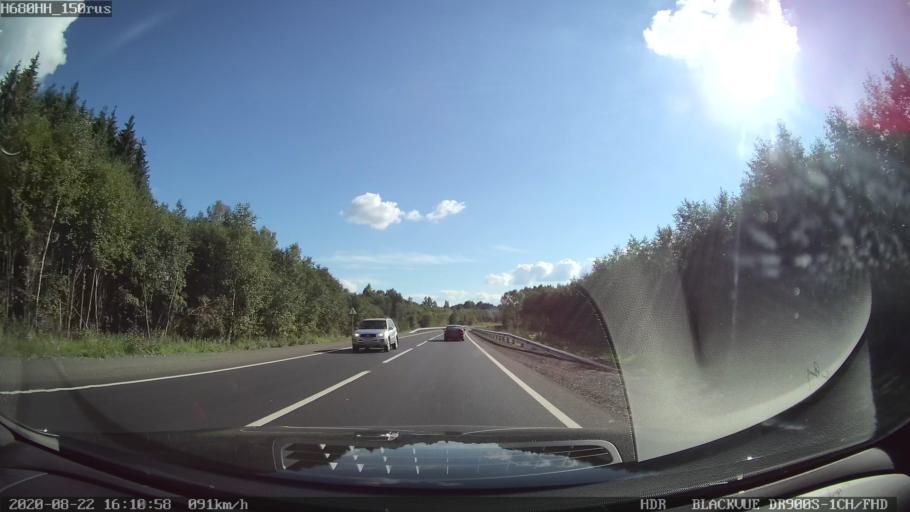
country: RU
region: Tverskaya
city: Rameshki
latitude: 57.5068
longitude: 36.2681
